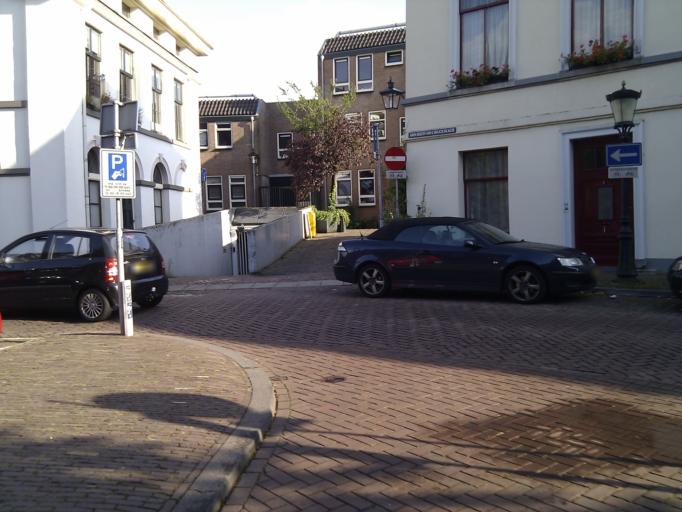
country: NL
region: Utrecht
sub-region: Gemeente Utrecht
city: Utrecht
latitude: 52.0962
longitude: 5.1203
